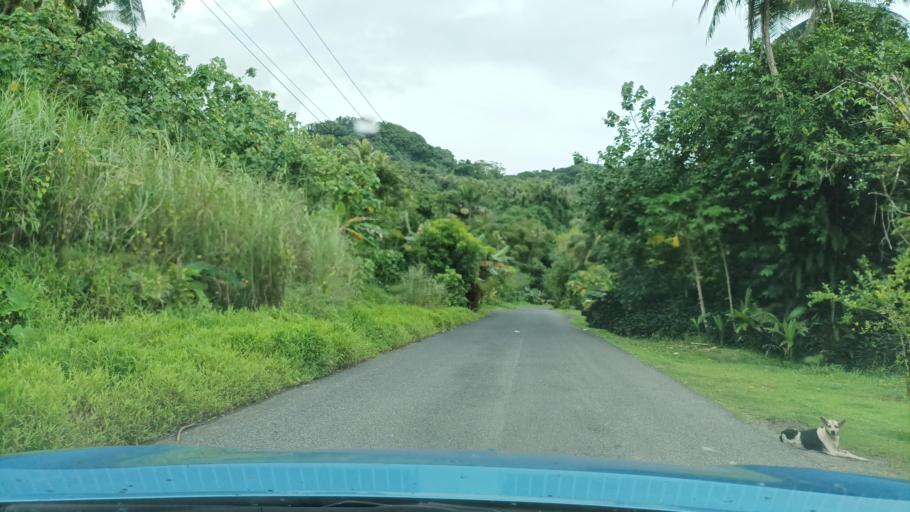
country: FM
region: Pohnpei
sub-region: Kolonia Municipality
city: Kolonia
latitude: 6.9464
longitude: 158.2750
